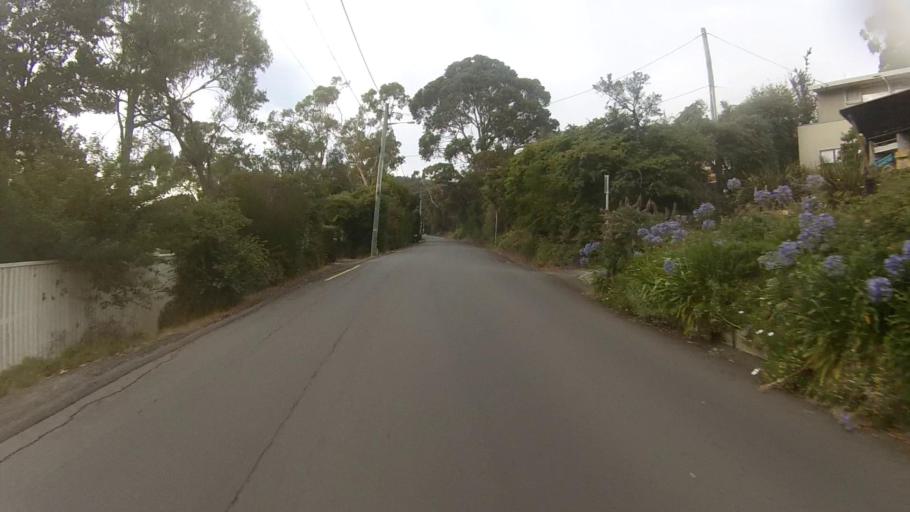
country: AU
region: Tasmania
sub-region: Hobart
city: Dynnyrne
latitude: -42.9086
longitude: 147.3285
